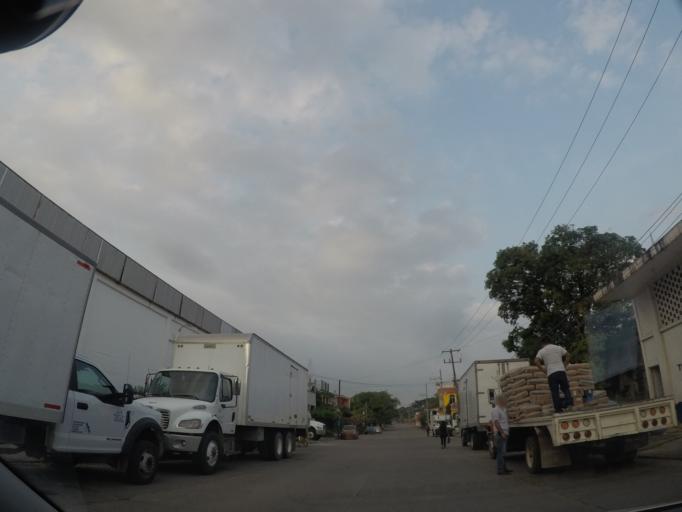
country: MX
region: Oaxaca
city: Matias Romero
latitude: 16.8762
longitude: -95.0436
